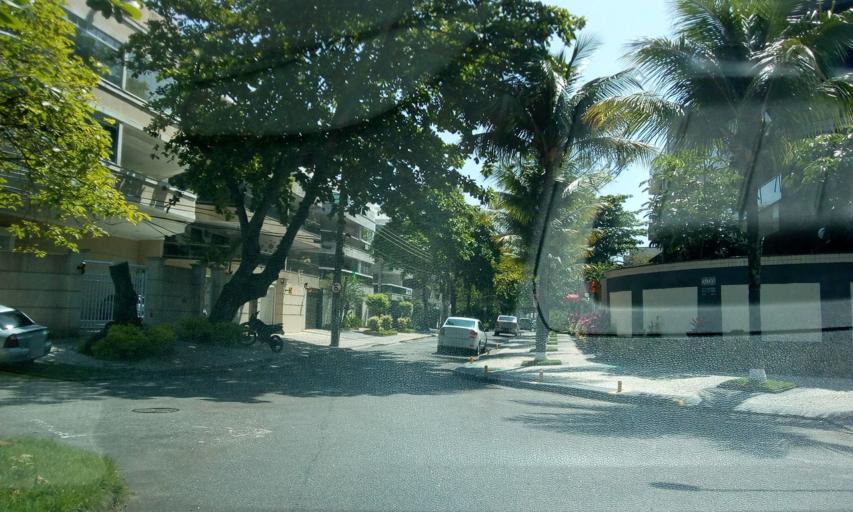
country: BR
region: Rio de Janeiro
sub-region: Nilopolis
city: Nilopolis
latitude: -23.0193
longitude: -43.4782
